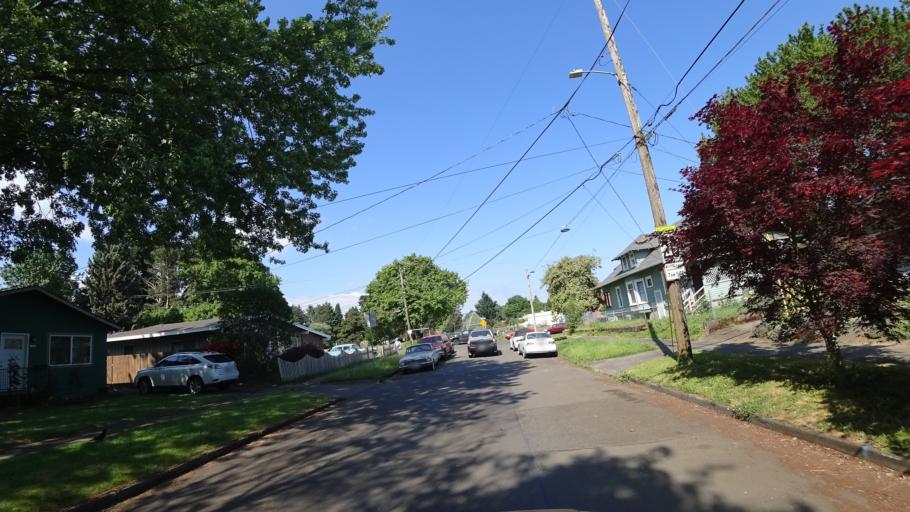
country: US
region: Oregon
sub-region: Multnomah County
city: Portland
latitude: 45.5741
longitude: -122.6512
